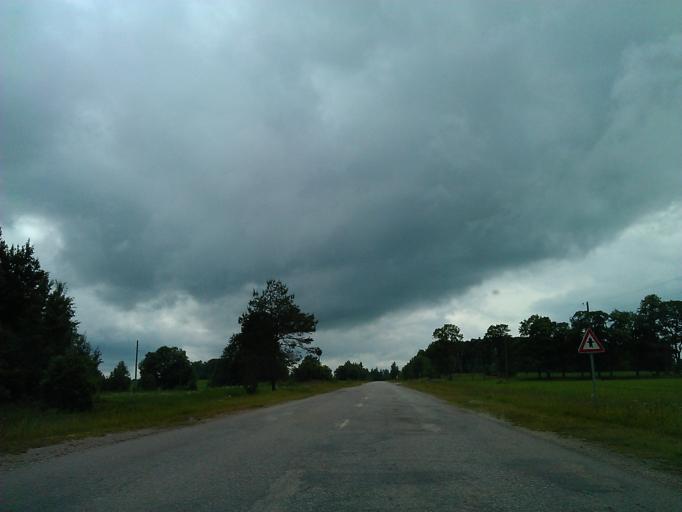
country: LV
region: Kuldigas Rajons
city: Kuldiga
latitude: 56.8577
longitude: 21.8171
